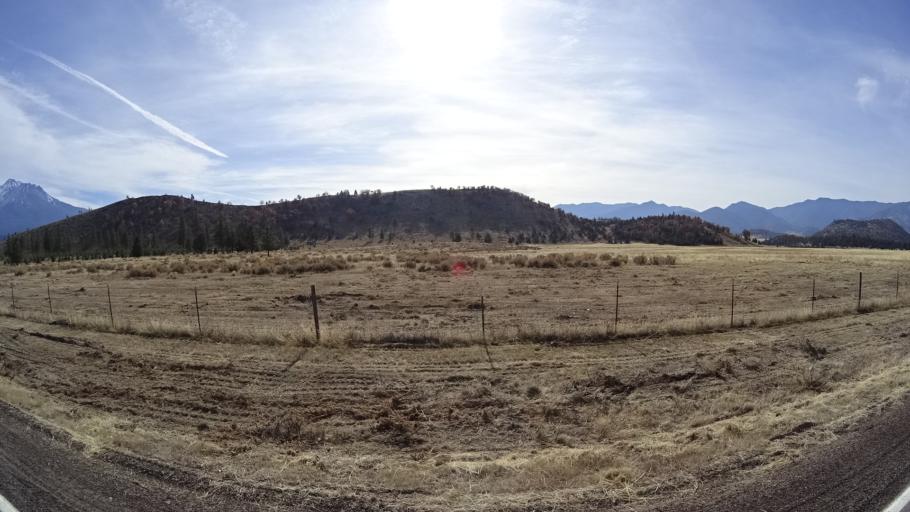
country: US
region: California
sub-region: Siskiyou County
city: Weed
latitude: 41.4940
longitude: -122.3995
